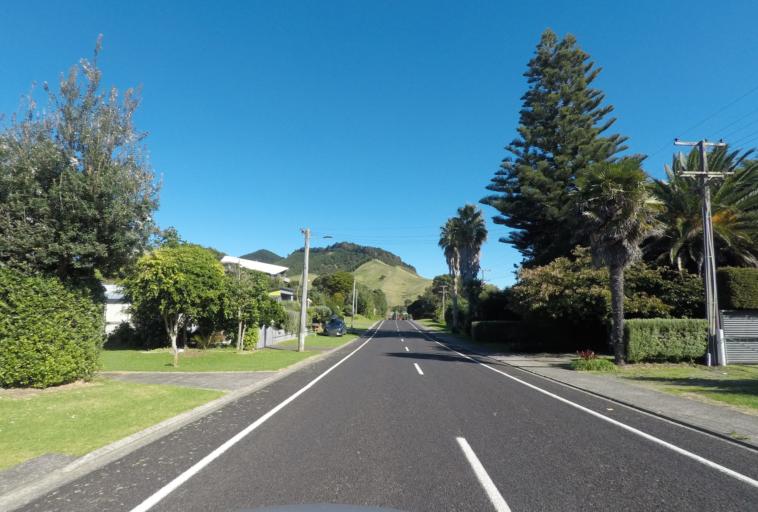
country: NZ
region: Waikato
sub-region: Thames-Coromandel District
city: Whangamata
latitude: -37.2831
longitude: 175.9002
